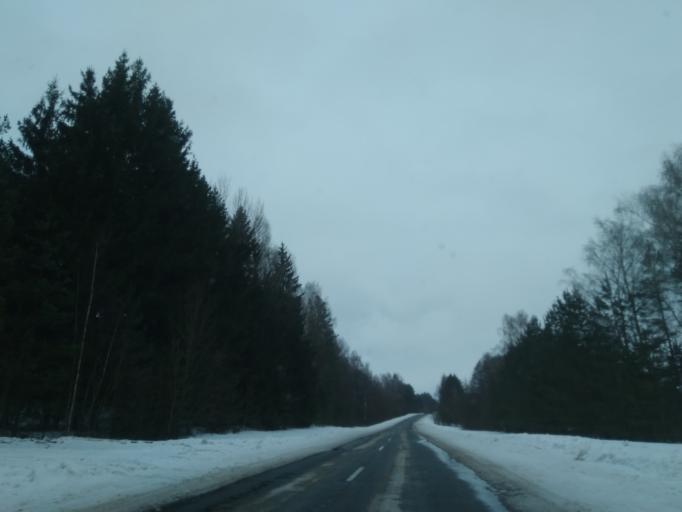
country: BY
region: Minsk
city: Ivyanyets
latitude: 53.8486
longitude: 26.7903
